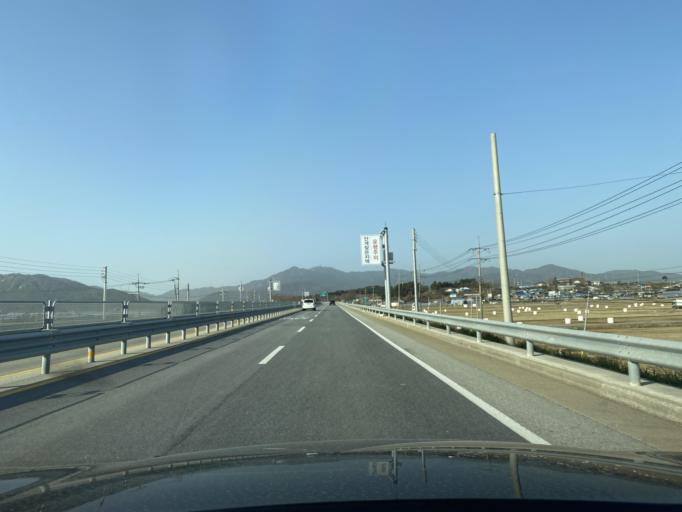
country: KR
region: Chungcheongnam-do
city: Hongsung
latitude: 36.6903
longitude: 126.7038
